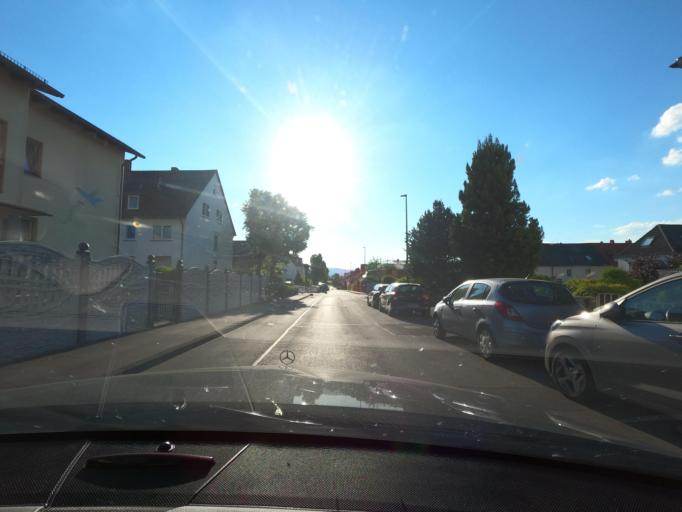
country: DE
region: Hesse
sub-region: Regierungsbezirk Kassel
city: Lohfelden
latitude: 51.3042
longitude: 9.5467
